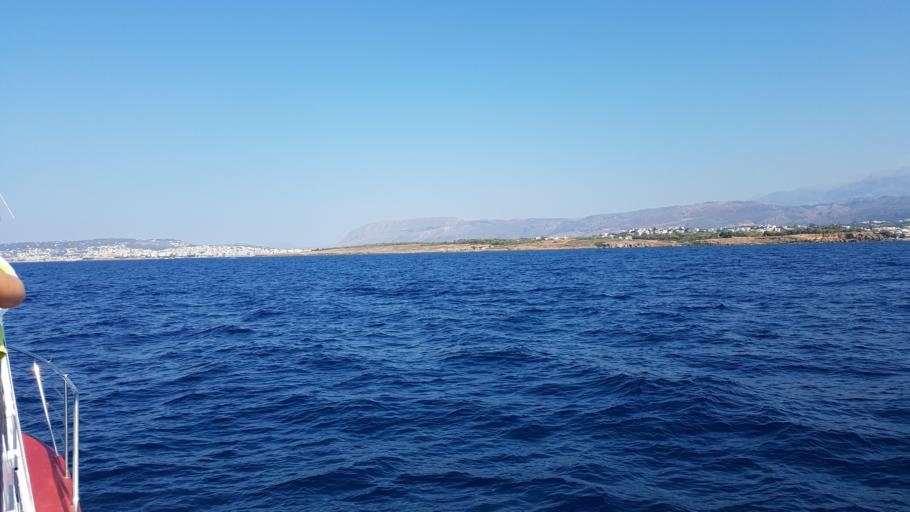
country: GR
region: Crete
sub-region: Nomos Chanias
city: Daratsos
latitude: 35.5230
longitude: 23.9714
